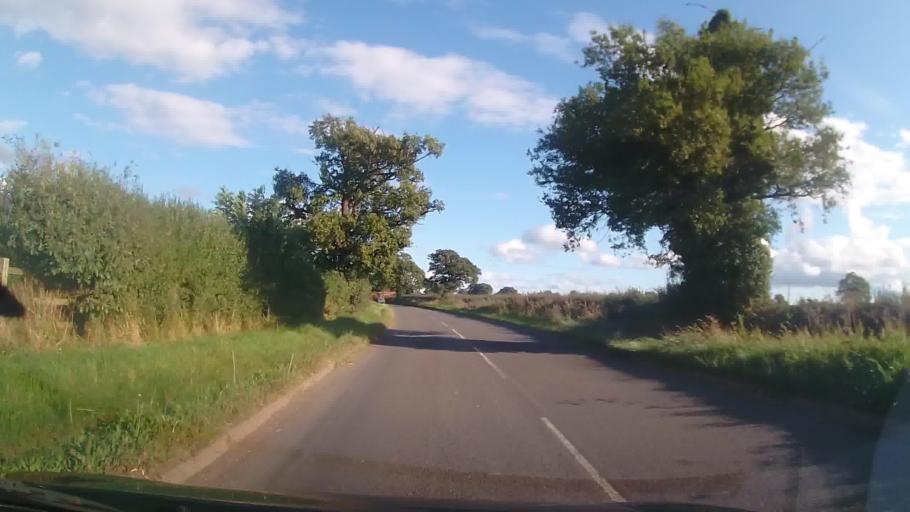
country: GB
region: England
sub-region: Shropshire
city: Great Hanwood
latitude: 52.6569
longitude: -2.8097
